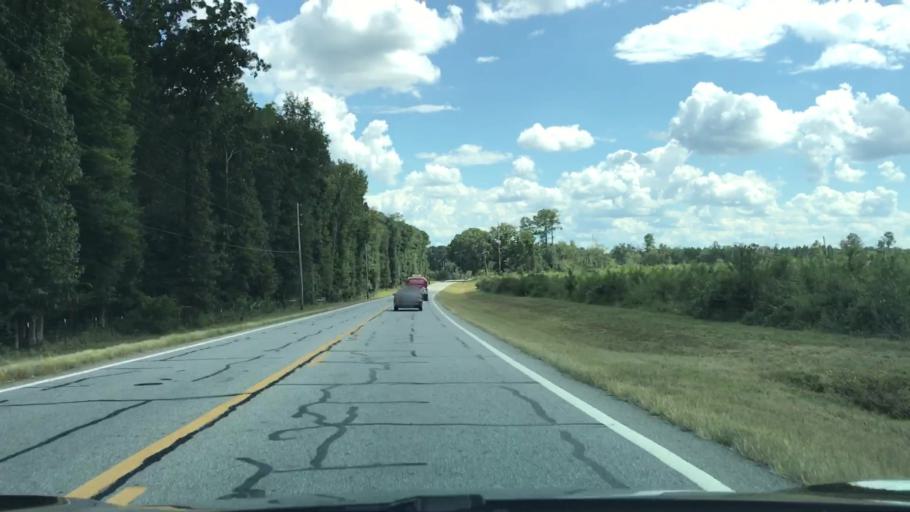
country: US
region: Georgia
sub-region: Oconee County
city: Watkinsville
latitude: 33.7896
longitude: -83.3205
